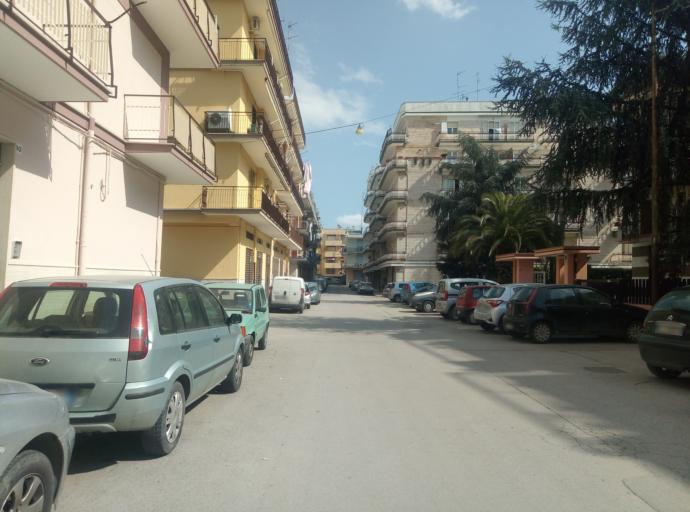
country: IT
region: Apulia
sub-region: Provincia di Bari
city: Ruvo di Puglia
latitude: 41.1169
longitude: 16.4791
